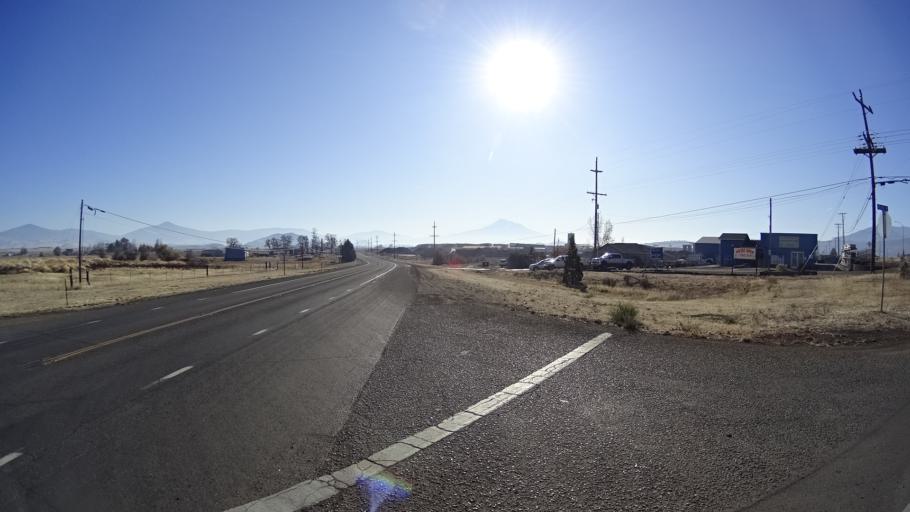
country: US
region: California
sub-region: Siskiyou County
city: Yreka
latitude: 41.7353
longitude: -122.5931
